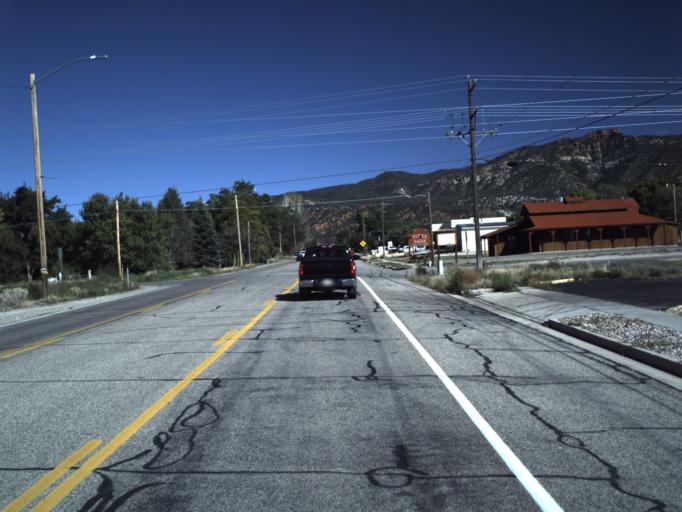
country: US
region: Utah
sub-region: Iron County
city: Parowan
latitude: 37.8387
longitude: -112.8406
